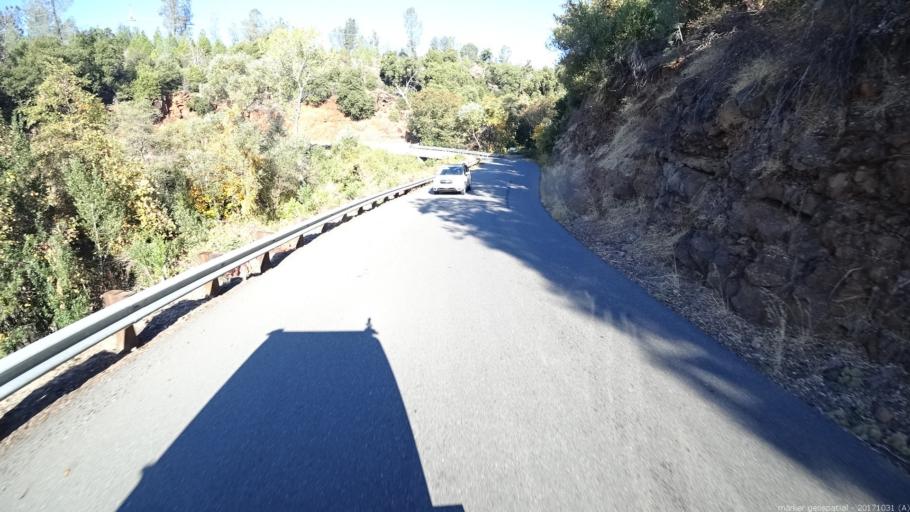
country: US
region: California
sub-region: Shasta County
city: Shingletown
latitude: 40.4463
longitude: -121.8680
